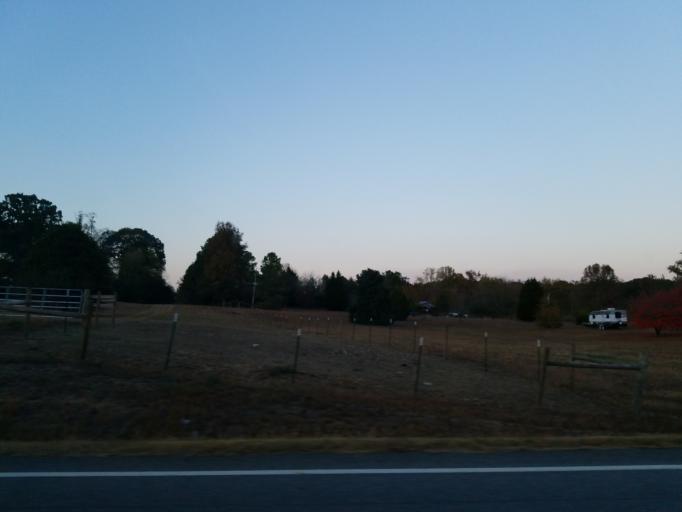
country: US
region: Georgia
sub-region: Gordon County
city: Calhoun
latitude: 34.5733
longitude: -84.9809
